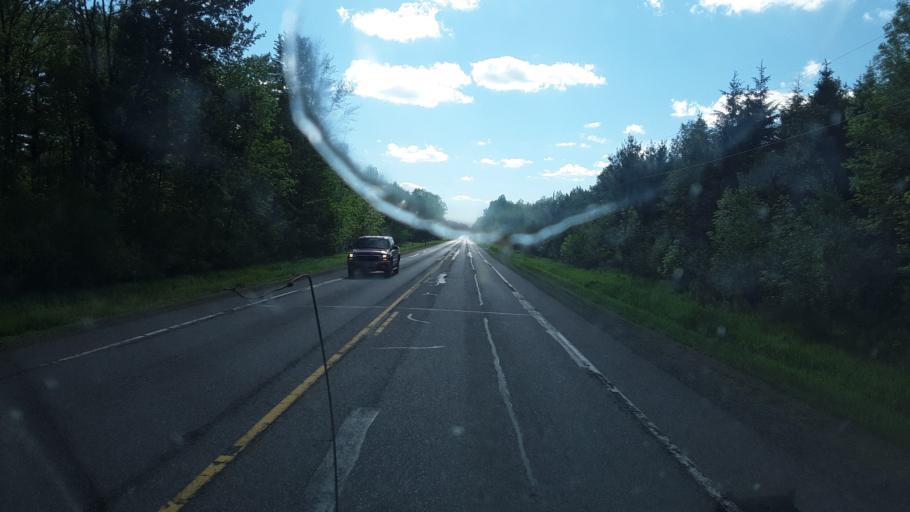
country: US
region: Wisconsin
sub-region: Wood County
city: Marshfield
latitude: 44.4537
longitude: -90.1639
